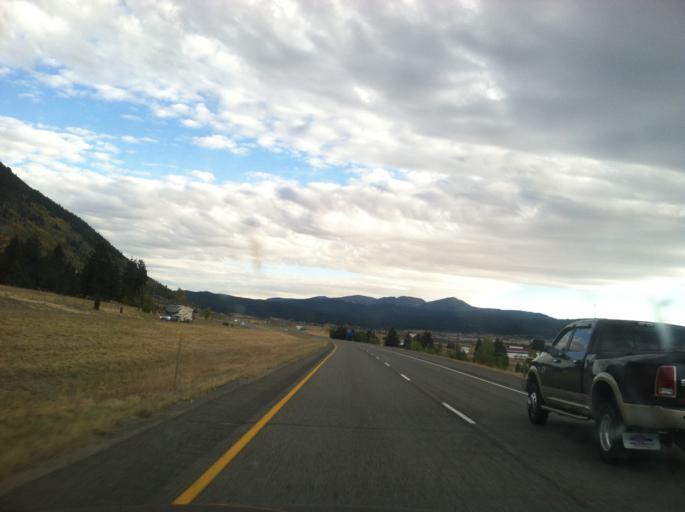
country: US
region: Montana
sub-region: Silver Bow County
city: Butte
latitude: 45.9713
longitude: -112.4758
